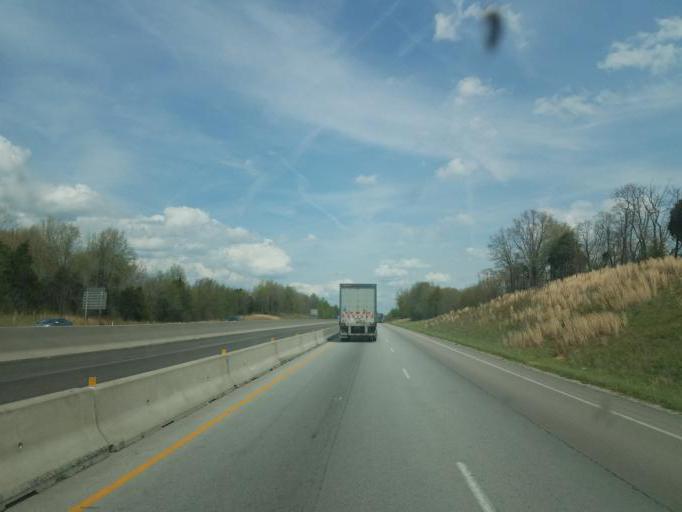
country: US
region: Kentucky
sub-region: Hardin County
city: Elizabethtown
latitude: 37.6021
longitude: -85.8673
